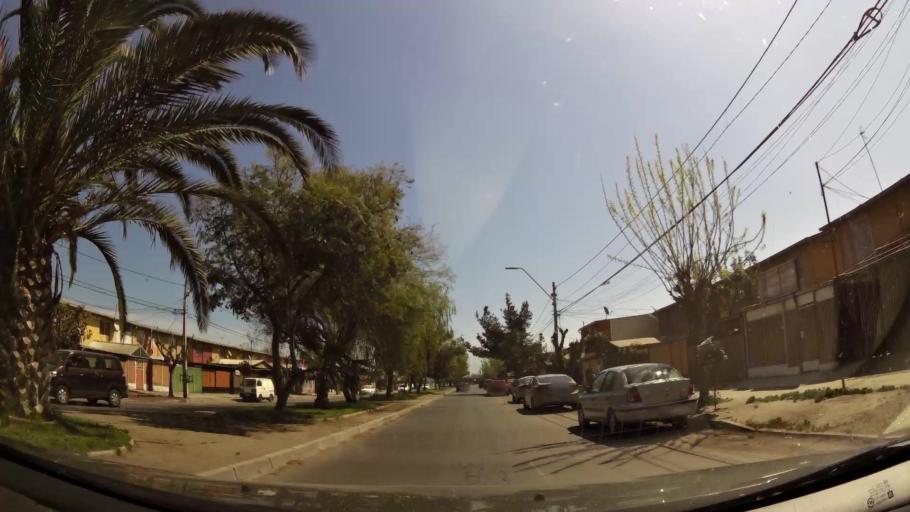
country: CL
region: Santiago Metropolitan
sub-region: Provincia de Santiago
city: Lo Prado
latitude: -33.4009
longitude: -70.7515
